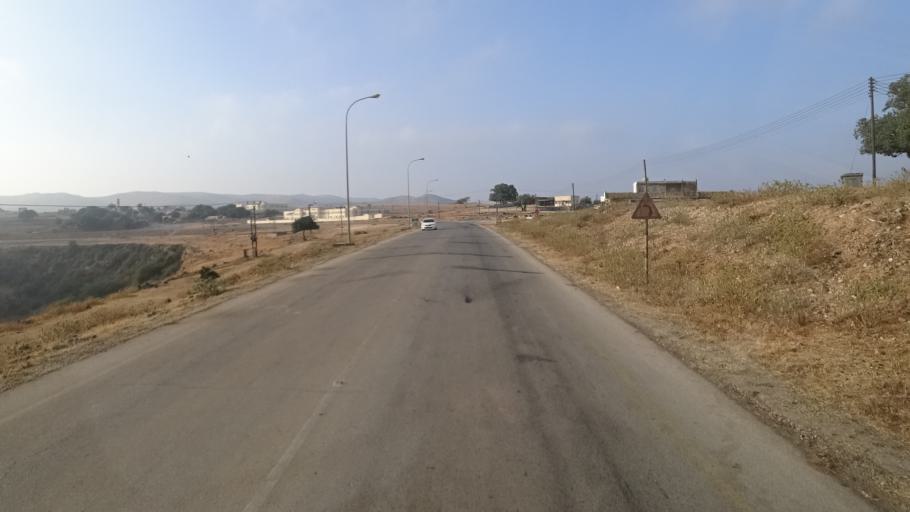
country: OM
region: Zufar
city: Salalah
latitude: 17.1234
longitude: 53.9993
